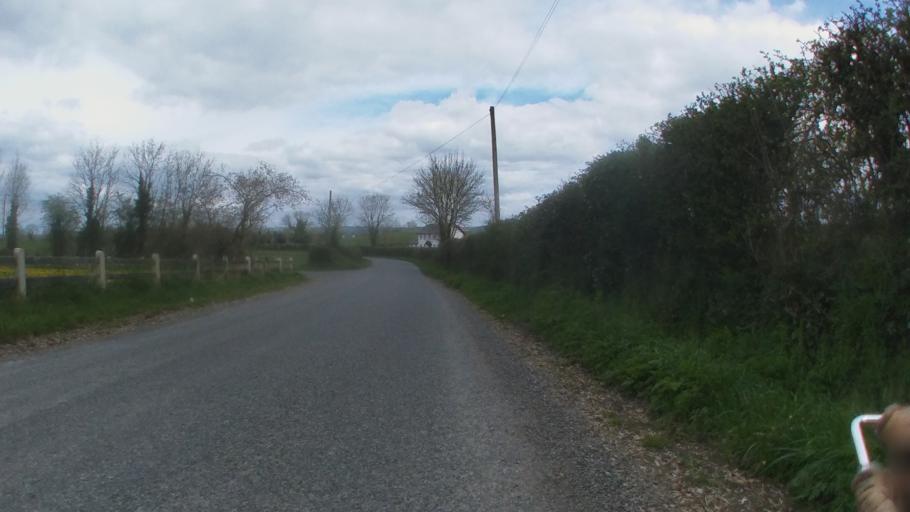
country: IE
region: Leinster
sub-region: Kilkenny
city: Kilkenny
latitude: 52.6524
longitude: -7.1837
